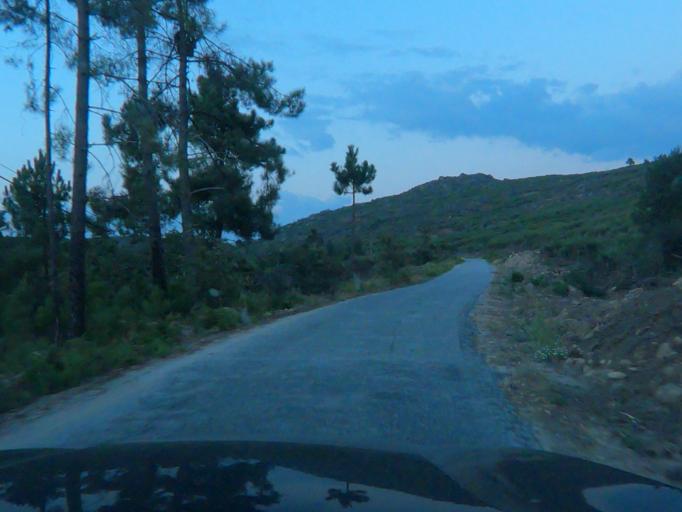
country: PT
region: Vila Real
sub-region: Sabrosa
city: Sabrosa
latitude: 41.2825
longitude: -7.6243
